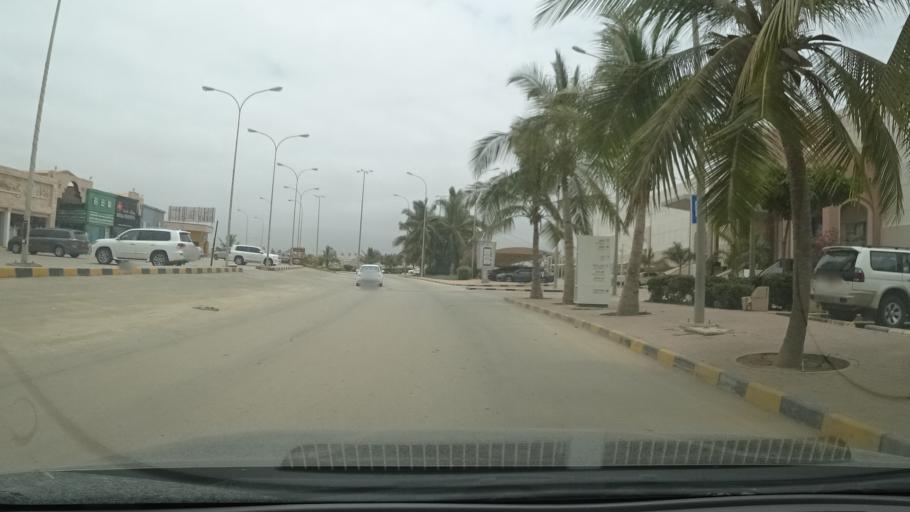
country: OM
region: Zufar
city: Salalah
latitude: 17.0223
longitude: 54.0647
